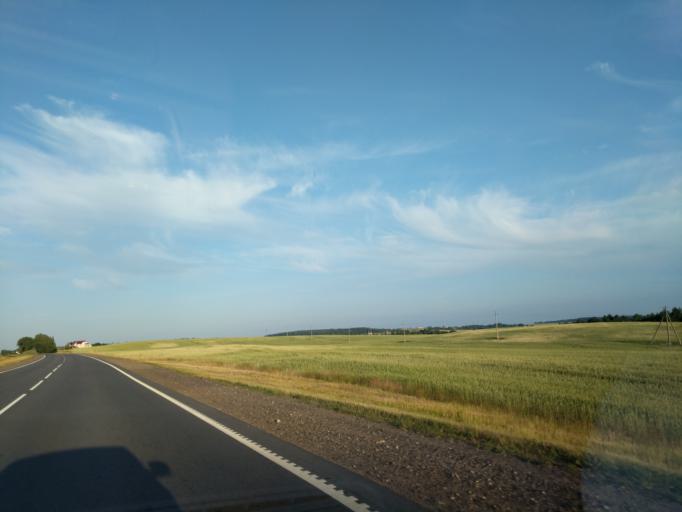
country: BY
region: Minsk
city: Syomkava
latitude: 54.1003
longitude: 27.4839
